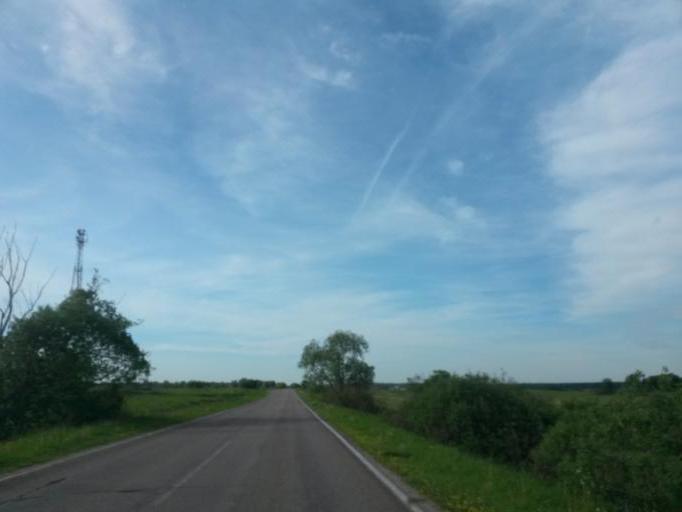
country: RU
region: Moskovskaya
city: Lyubuchany
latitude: 55.2350
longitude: 37.6440
